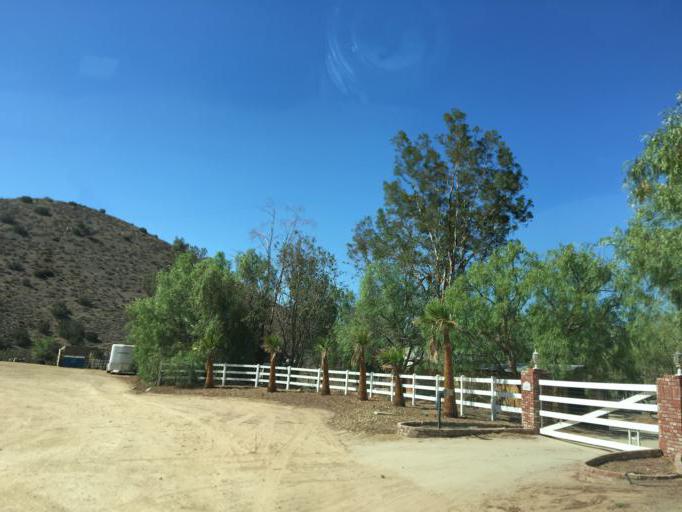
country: US
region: California
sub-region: Los Angeles County
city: Acton
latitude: 34.5044
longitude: -118.1919
